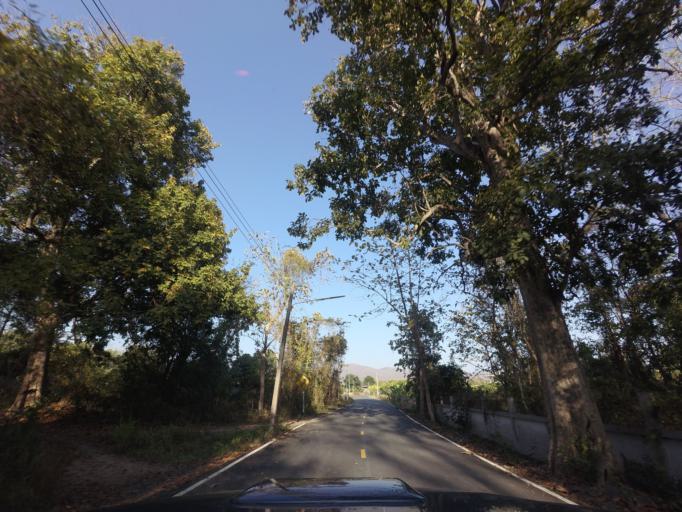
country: TH
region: Chiang Mai
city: San Sai
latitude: 18.9033
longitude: 99.1230
